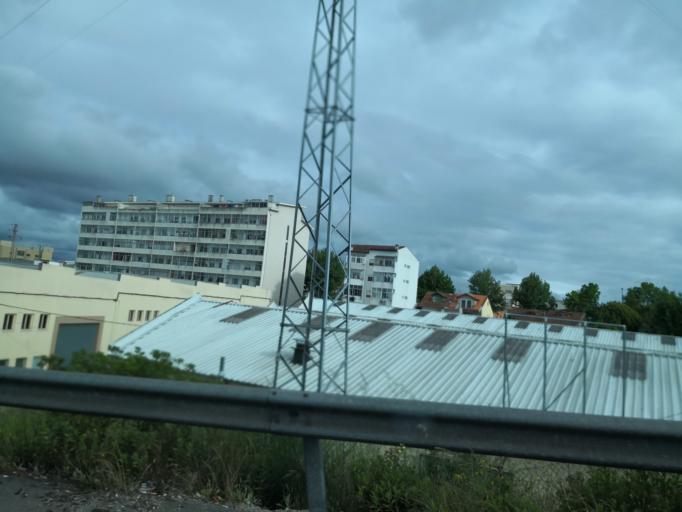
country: PT
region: Porto
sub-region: Gondomar
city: Rio Tinto
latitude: 41.1687
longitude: -8.5700
